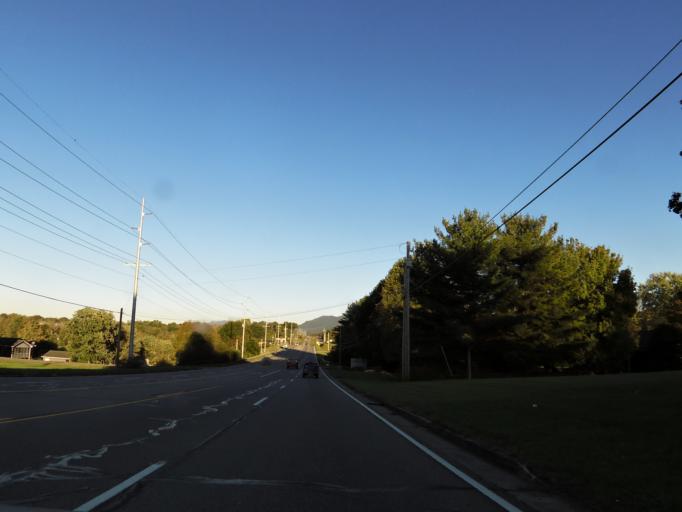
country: US
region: Tennessee
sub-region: Blount County
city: Wildwood
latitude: 35.7577
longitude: -83.8880
